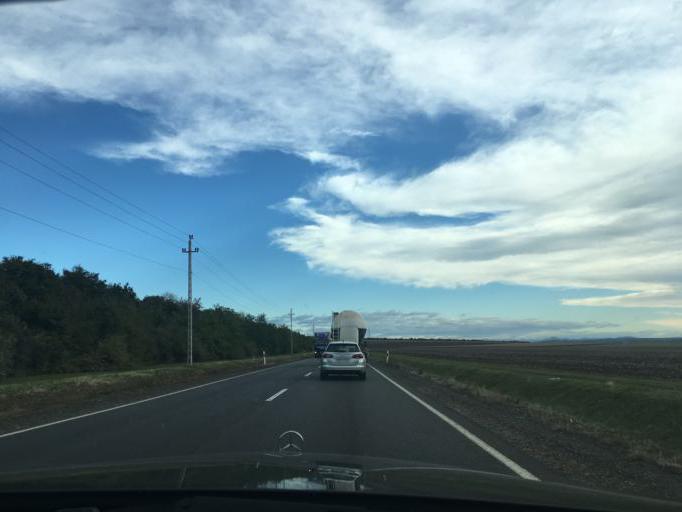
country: HU
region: Borsod-Abauj-Zemplen
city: Arnot
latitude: 48.1333
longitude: 20.8786
